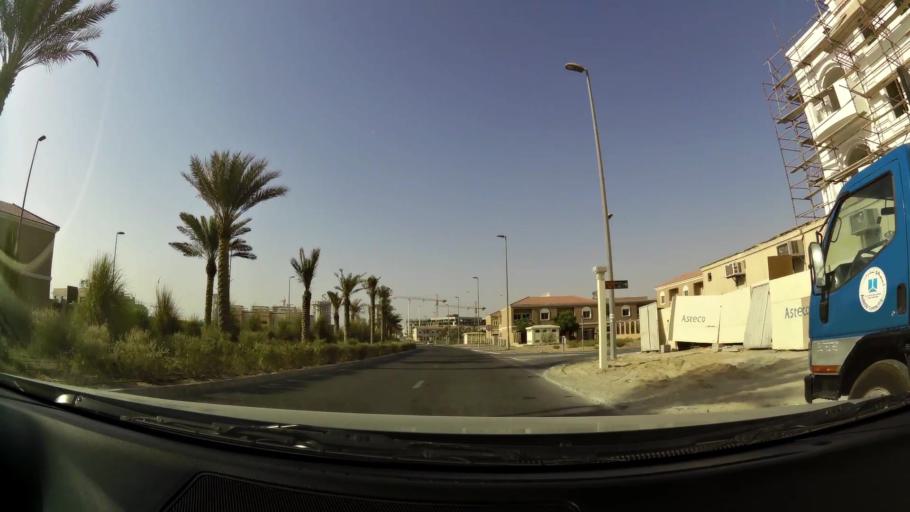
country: AE
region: Dubai
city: Dubai
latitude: 25.0534
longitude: 55.2152
